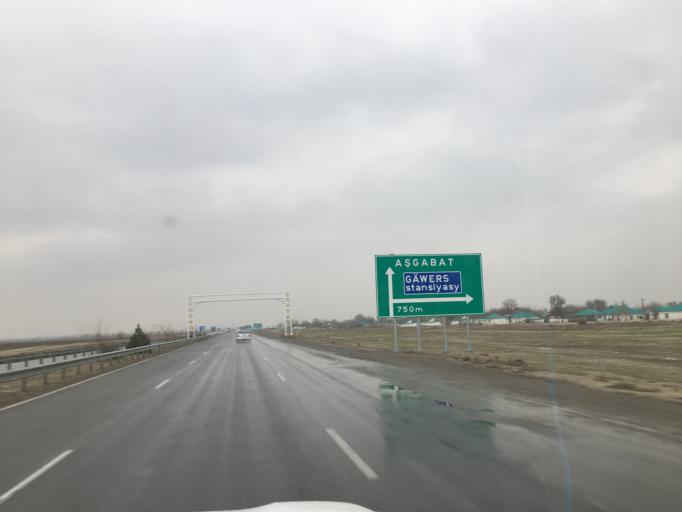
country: TM
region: Ahal
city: Annau
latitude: 37.8255
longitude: 58.7551
